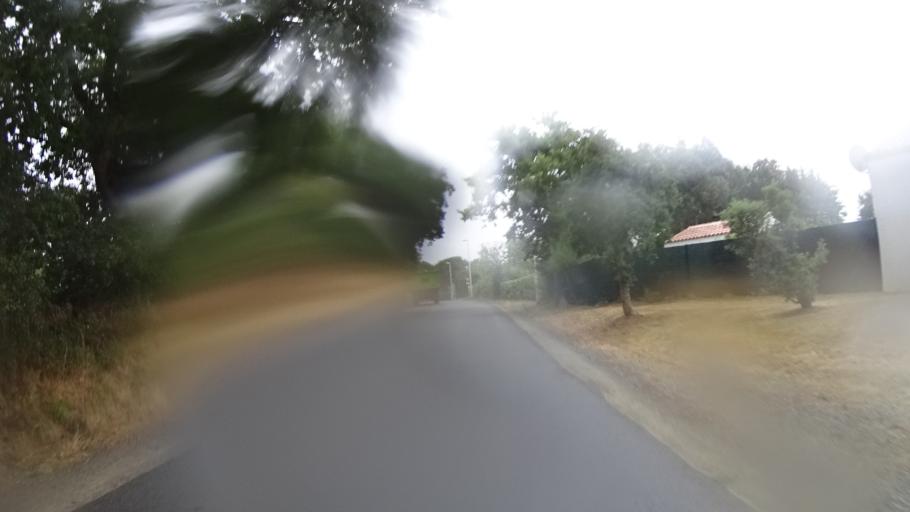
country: FR
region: Pays de la Loire
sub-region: Departement de la Loire-Atlantique
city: Saint-Brevin-les-Pins
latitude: 47.2619
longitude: -2.1398
